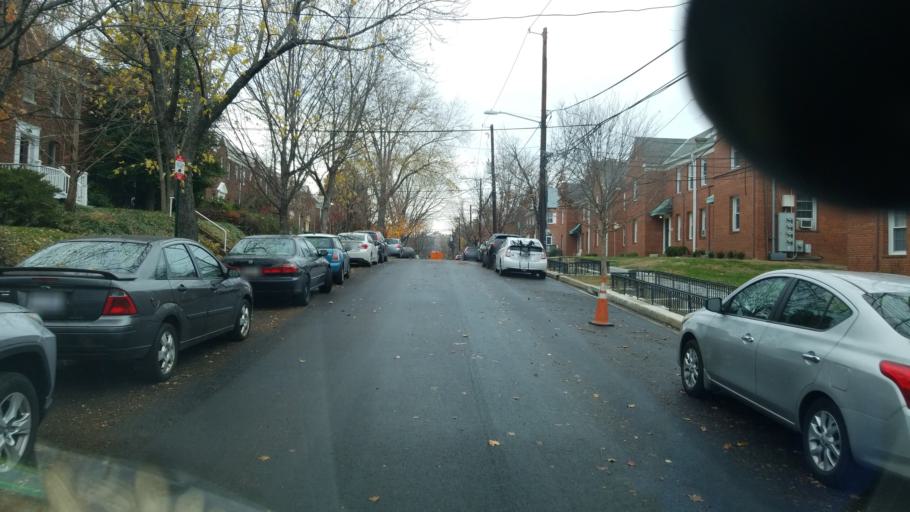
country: US
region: Maryland
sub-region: Montgomery County
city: Friendship Village
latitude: 38.9196
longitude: -77.0788
